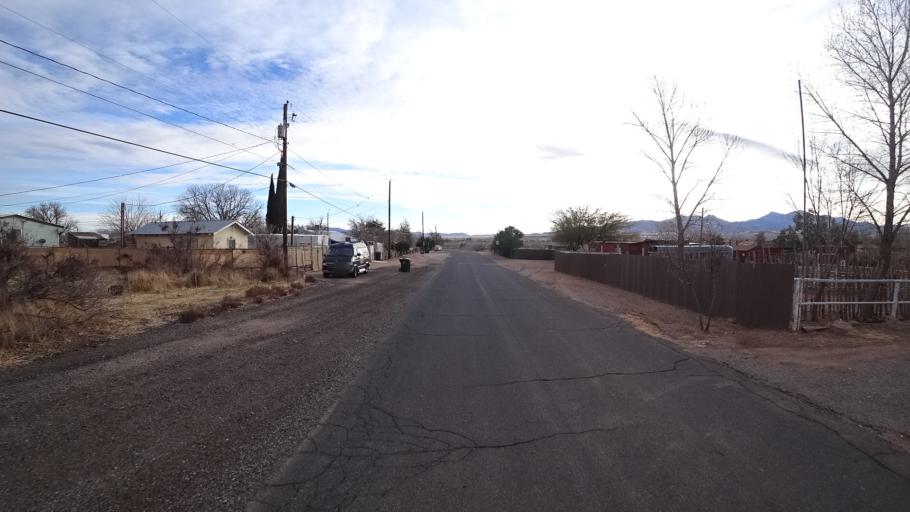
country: US
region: Arizona
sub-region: Mohave County
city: Kingman
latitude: 35.2149
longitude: -114.0500
